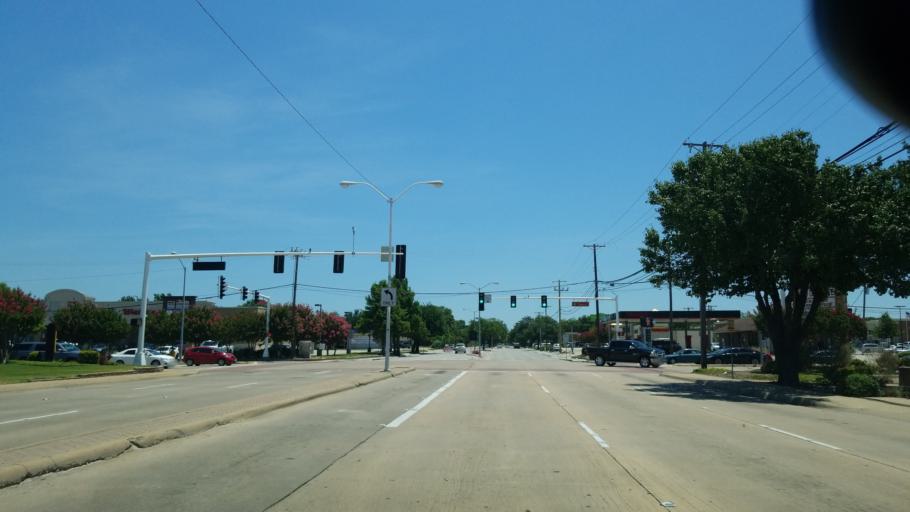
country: US
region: Texas
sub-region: Dallas County
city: Farmers Branch
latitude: 32.9244
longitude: -96.8823
